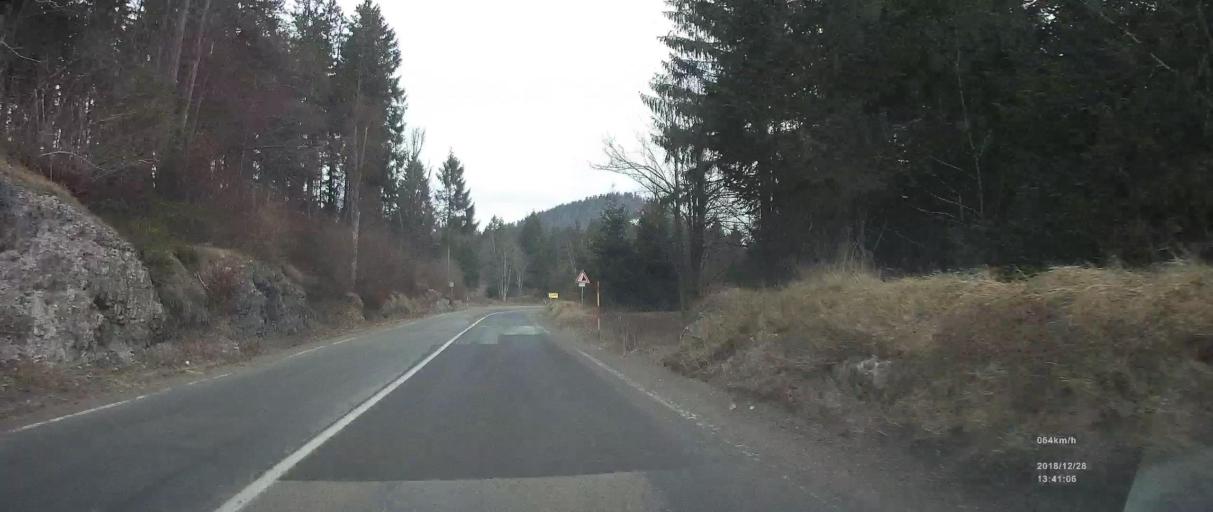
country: HR
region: Primorsko-Goranska
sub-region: Grad Delnice
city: Delnice
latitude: 45.3520
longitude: 14.7554
